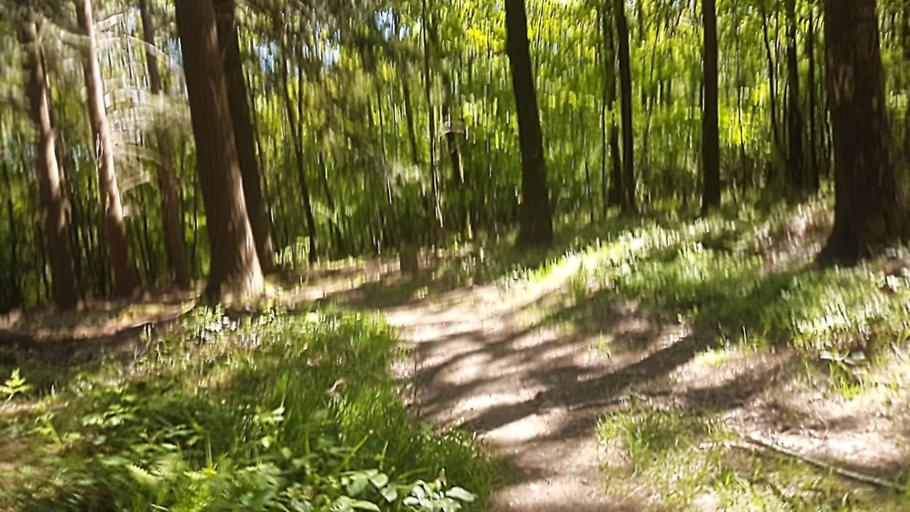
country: BE
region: Wallonia
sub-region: Province de Namur
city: Couvin
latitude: 50.0540
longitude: 4.5824
